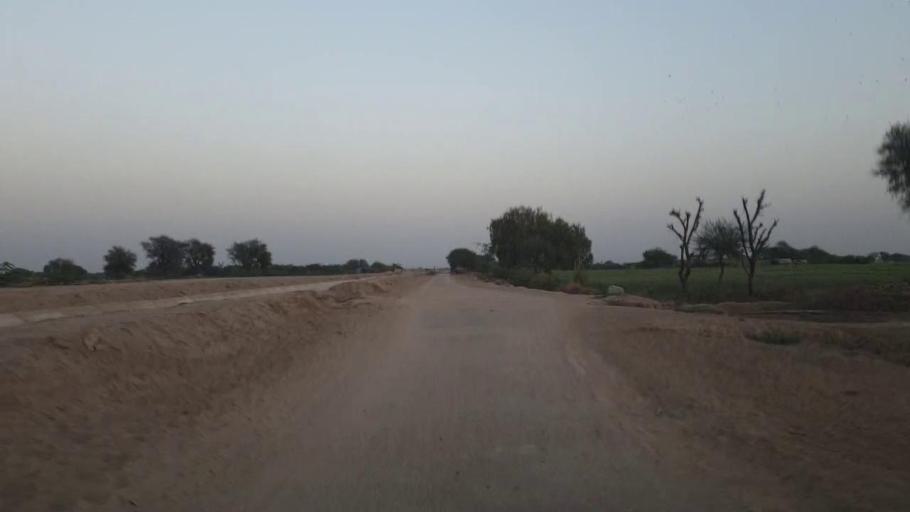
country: PK
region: Sindh
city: Umarkot
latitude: 25.4114
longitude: 69.6803
